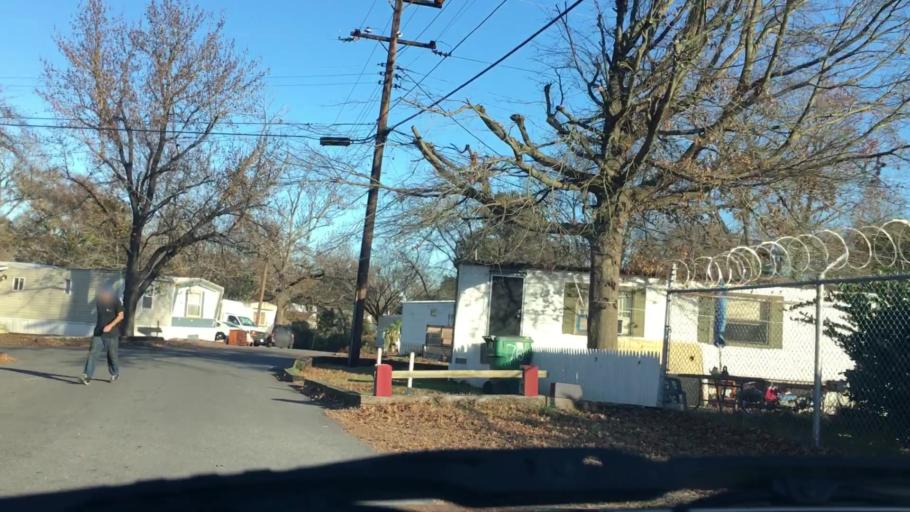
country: US
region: Virginia
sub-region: City of Norfolk
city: Norfolk
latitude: 36.8829
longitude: -76.2516
